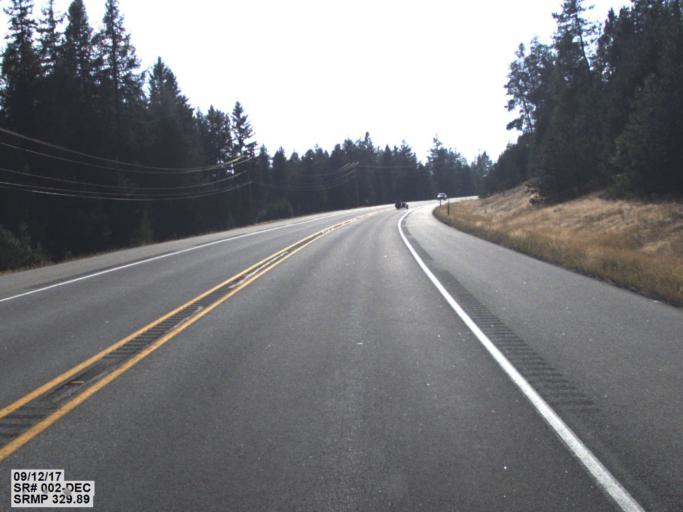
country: US
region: Washington
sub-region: Pend Oreille County
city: Newport
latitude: 48.1496
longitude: -117.1163
